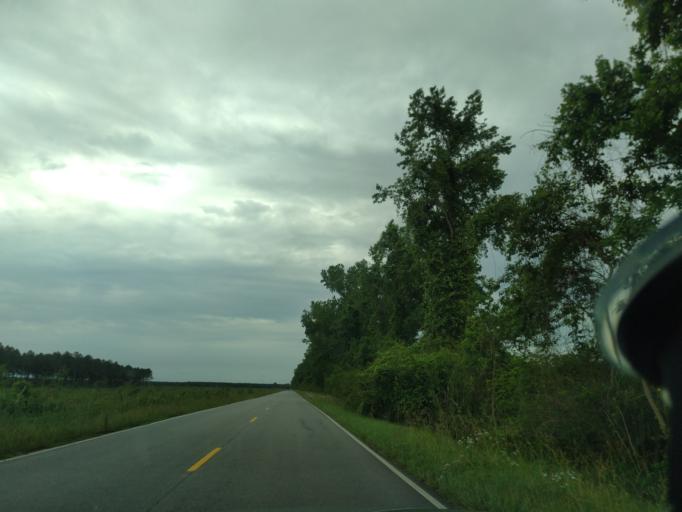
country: US
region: North Carolina
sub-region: Washington County
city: Plymouth
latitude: 35.8681
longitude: -76.5896
